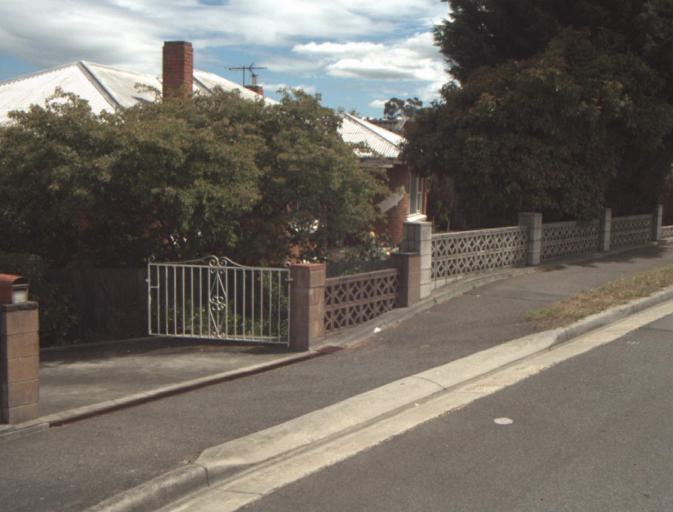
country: AU
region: Tasmania
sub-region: Launceston
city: Invermay
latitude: -41.3928
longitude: 147.1254
